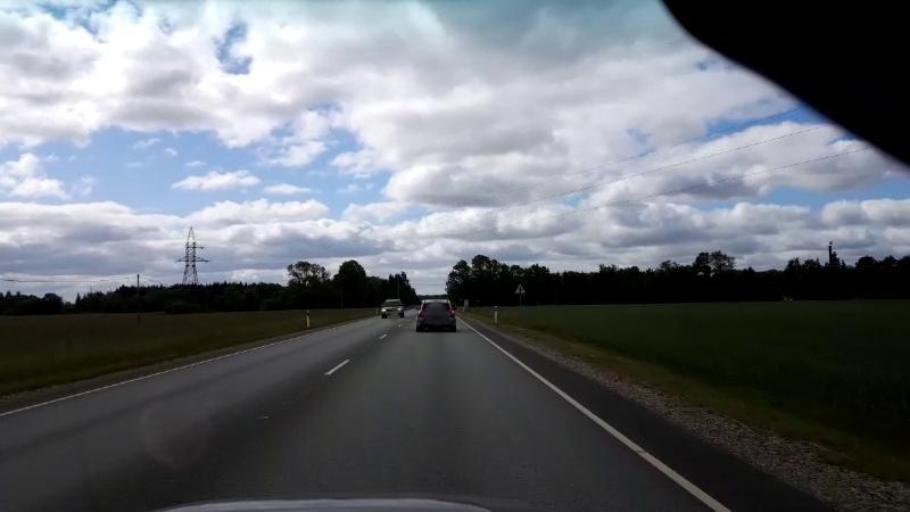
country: EE
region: Paernumaa
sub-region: Halinga vald
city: Parnu-Jaagupi
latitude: 58.5783
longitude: 24.5123
